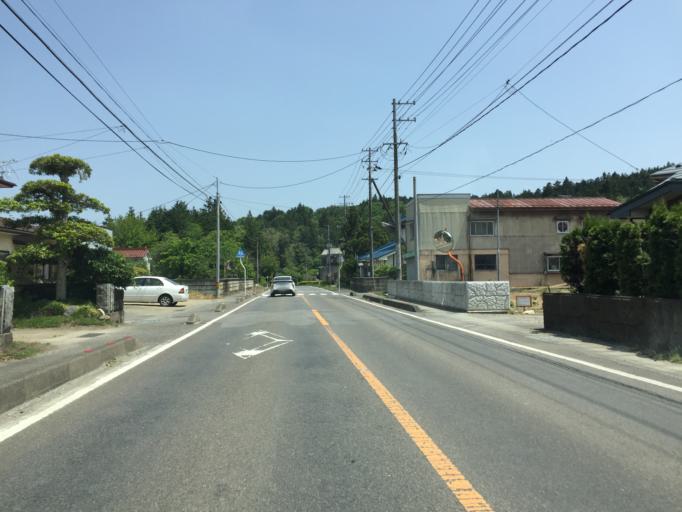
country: JP
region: Fukushima
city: Ishikawa
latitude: 37.1140
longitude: 140.3355
